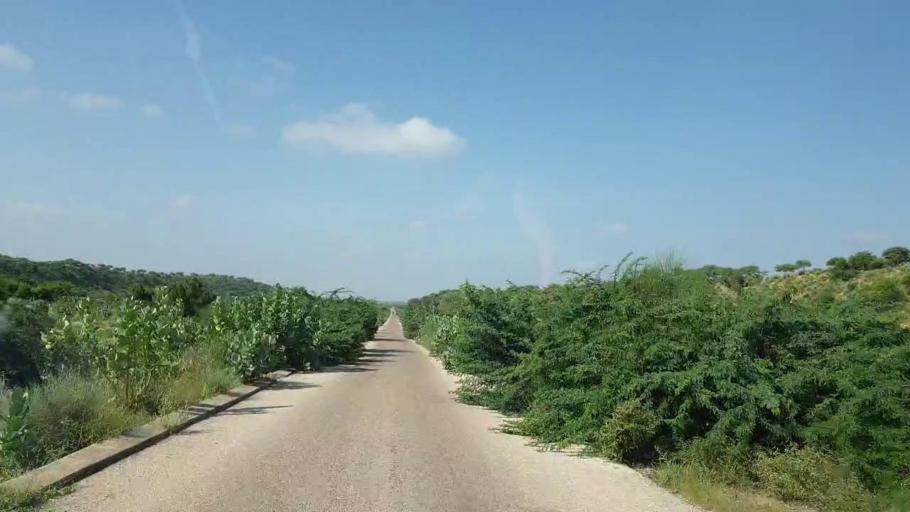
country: PK
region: Sindh
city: Mithi
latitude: 24.5429
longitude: 69.8713
